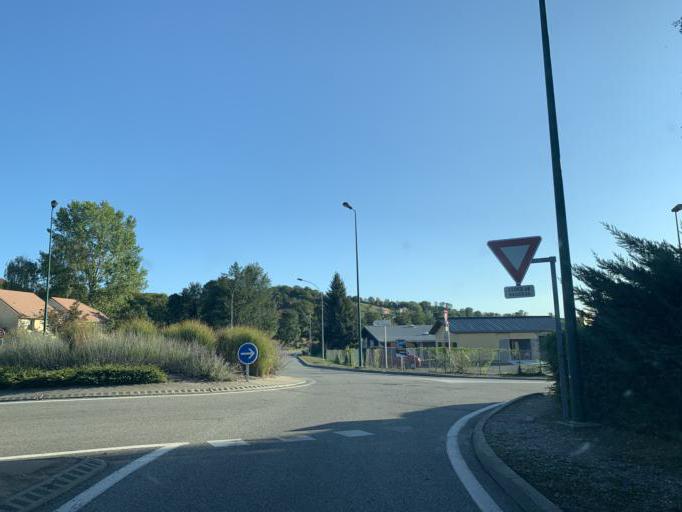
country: FR
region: Rhone-Alpes
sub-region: Departement de l'Ain
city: Belley
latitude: 45.7450
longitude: 5.6810
